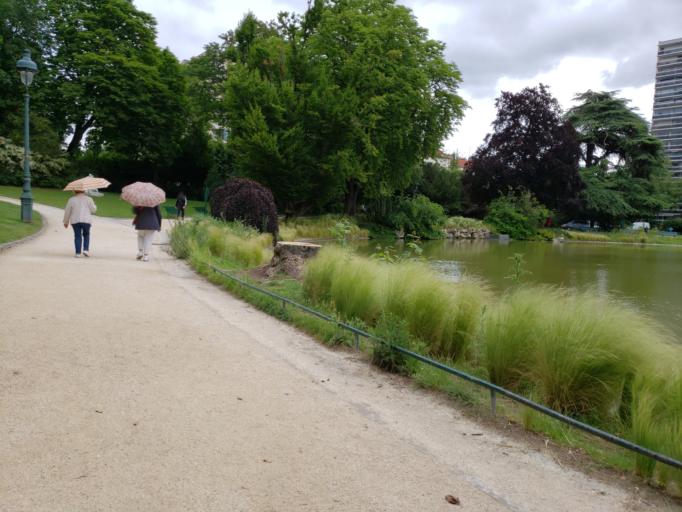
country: FR
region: Ile-de-France
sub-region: Departement du Val-de-Marne
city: Gentilly
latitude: 48.8237
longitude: 2.3383
